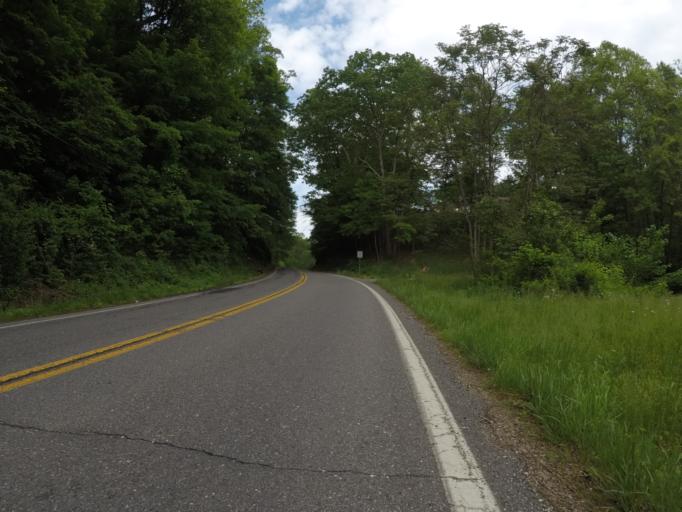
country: US
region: West Virginia
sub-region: Wayne County
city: Ceredo
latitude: 38.3551
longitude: -82.5497
